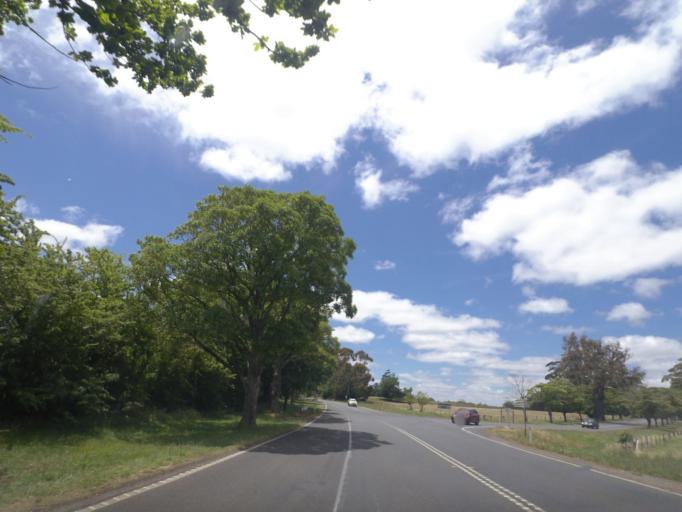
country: AU
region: Victoria
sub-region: Mount Alexander
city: Castlemaine
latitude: -37.3353
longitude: 144.1648
